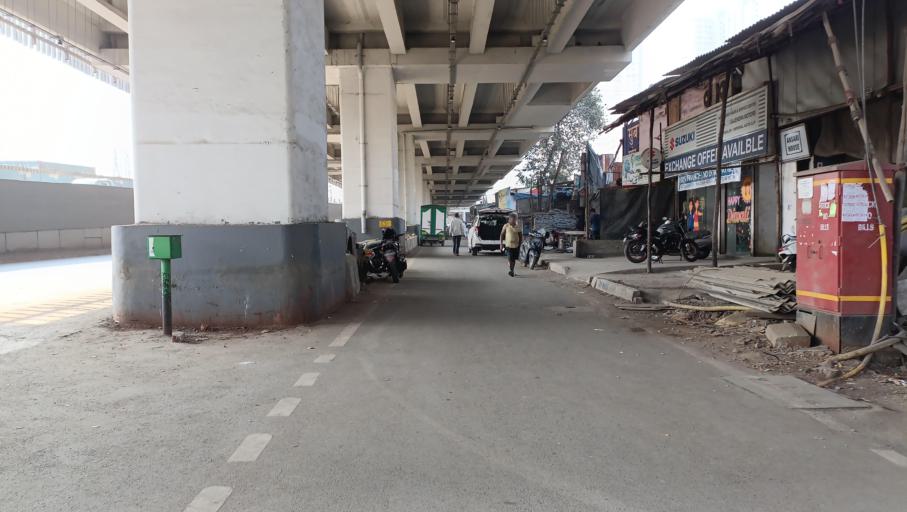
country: IN
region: Maharashtra
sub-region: Mumbai Suburban
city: Borivli
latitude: 19.2516
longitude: 72.8671
